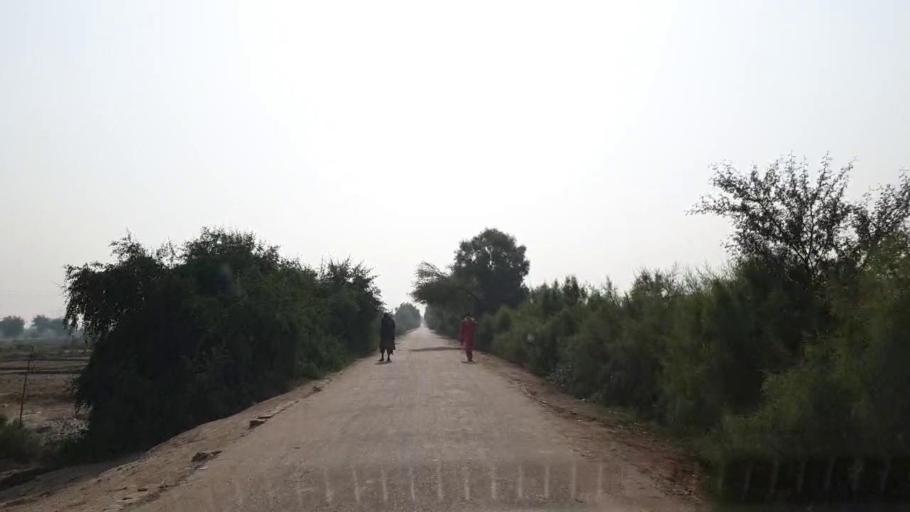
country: PK
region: Sindh
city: Bhan
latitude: 26.4785
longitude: 67.7714
